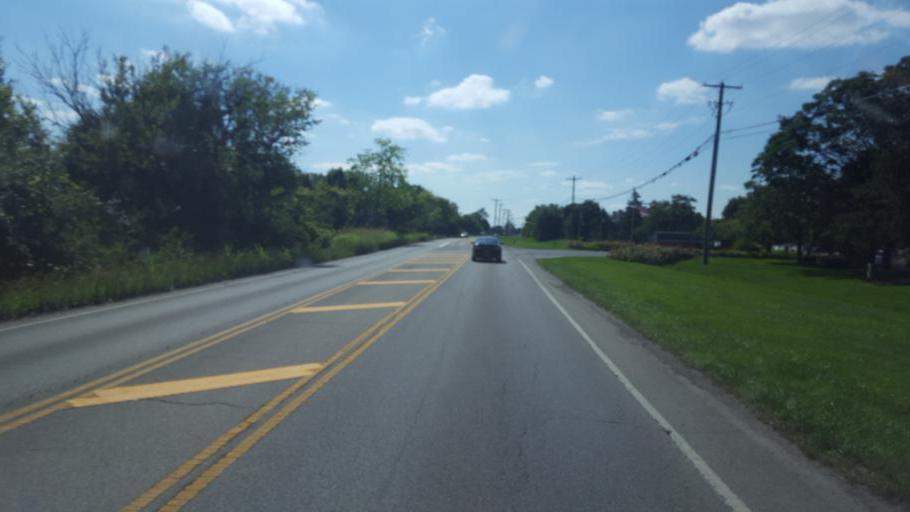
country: US
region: Ohio
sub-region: Franklin County
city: Dublin
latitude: 40.0921
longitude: -83.0773
